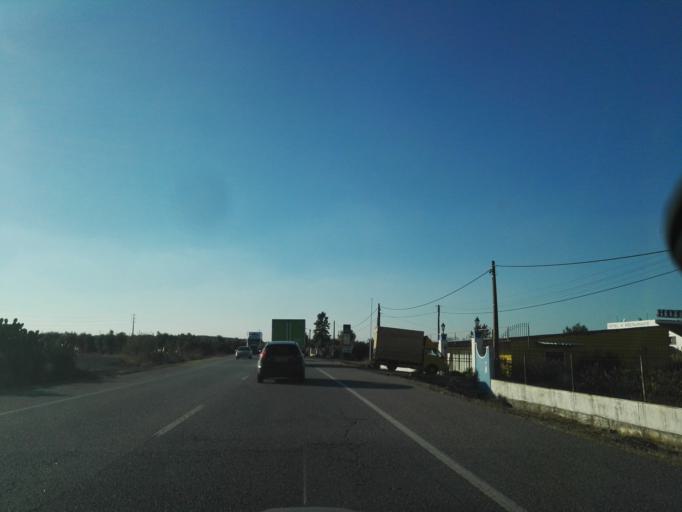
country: PT
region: Evora
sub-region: Borba
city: Borba
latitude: 38.8197
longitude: -7.4899
